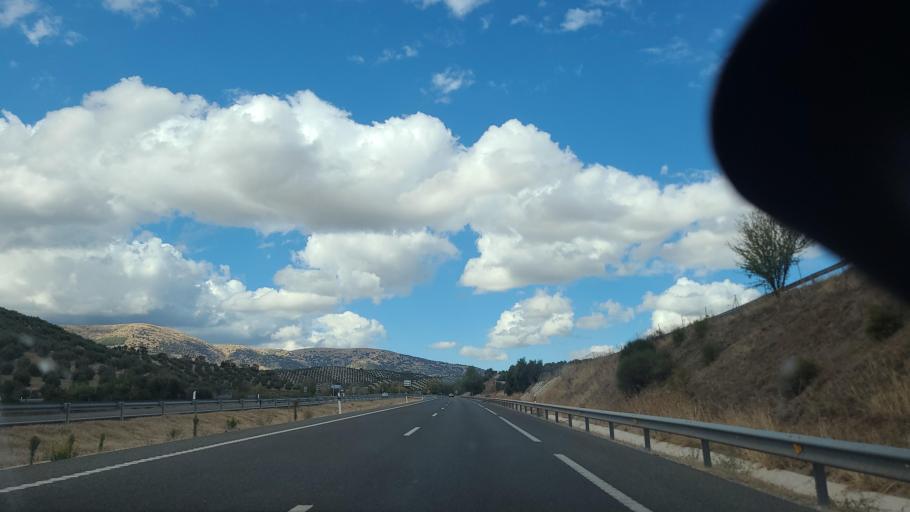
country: ES
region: Andalusia
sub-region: Provincia de Granada
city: Campotejar
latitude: 37.5075
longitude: -3.6321
